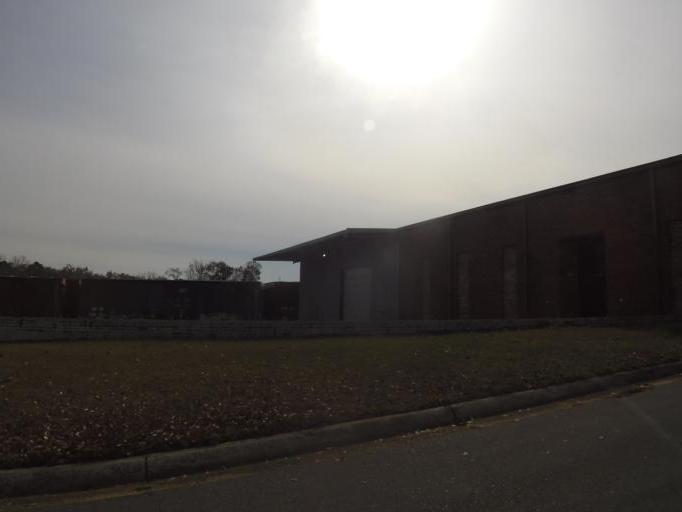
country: US
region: Alabama
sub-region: Houston County
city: Dothan
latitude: 31.2254
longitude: -85.3859
